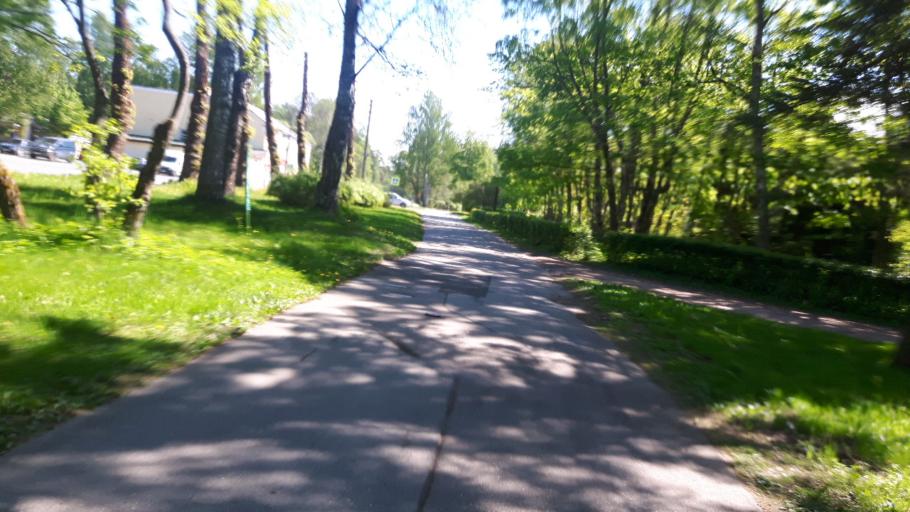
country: RU
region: St.-Petersburg
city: Zelenogorsk
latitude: 60.1926
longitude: 29.6890
